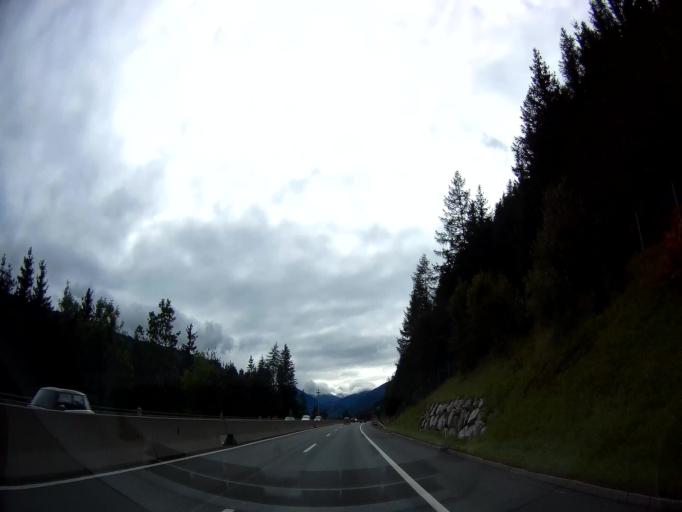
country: AT
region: Tyrol
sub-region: Politischer Bezirk Innsbruck Land
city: Matrei am Brenner
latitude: 47.1491
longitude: 11.4431
